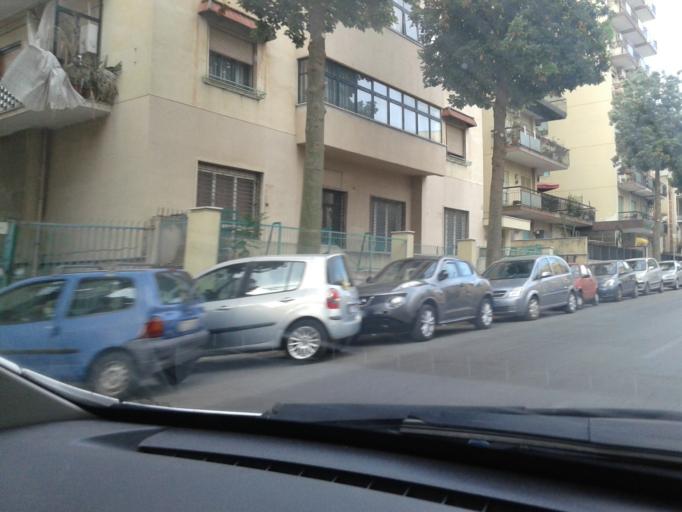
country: IT
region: Sicily
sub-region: Palermo
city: Palermo
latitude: 38.1105
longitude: 13.3356
